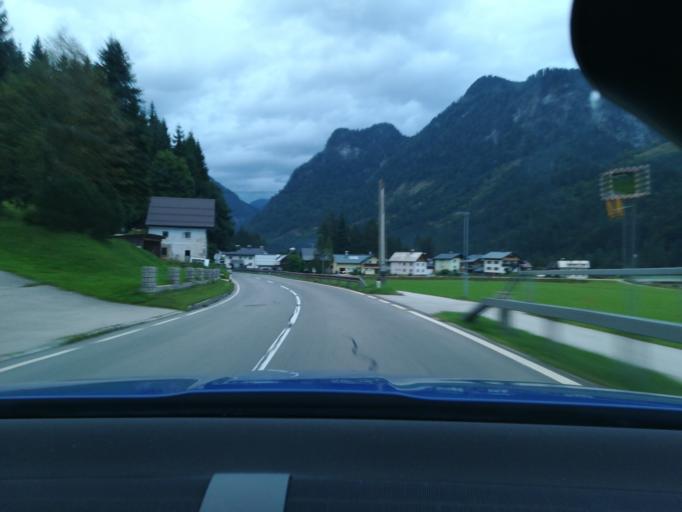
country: AT
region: Upper Austria
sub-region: Politischer Bezirk Gmunden
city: Bad Goisern
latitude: 47.5884
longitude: 13.5613
